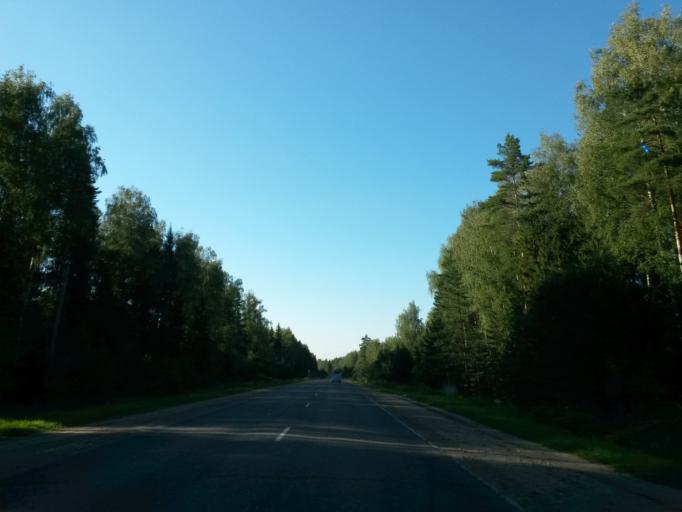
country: RU
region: Ivanovo
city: Novo-Talitsy
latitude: 57.0460
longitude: 40.7392
